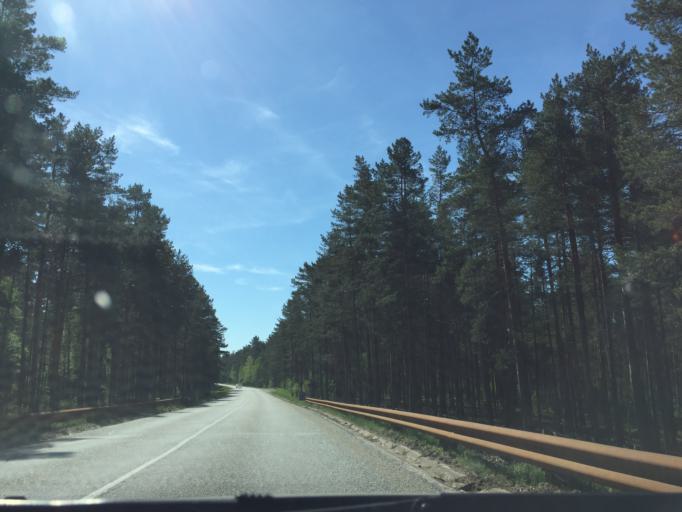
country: LV
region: Garkalne
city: Garkalne
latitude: 57.0380
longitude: 24.4165
